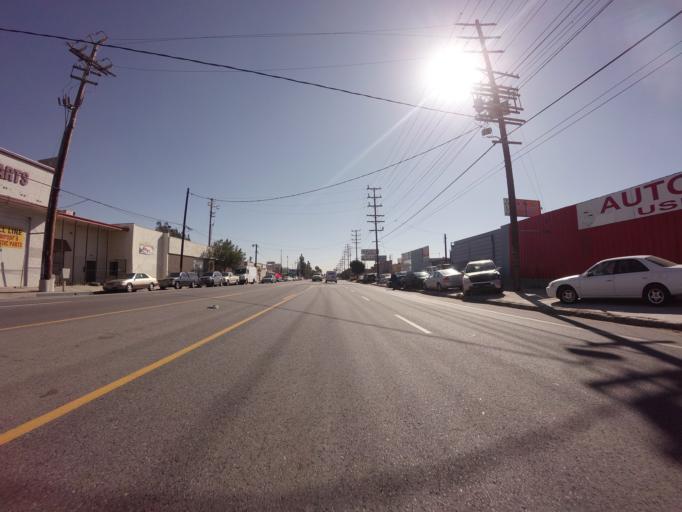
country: US
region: California
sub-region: Los Angeles County
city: North Hollywood
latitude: 34.2387
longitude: -118.3758
